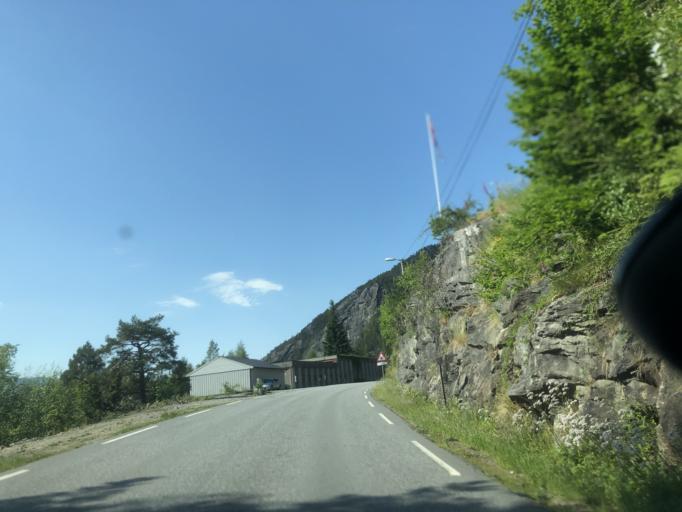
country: NO
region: Hordaland
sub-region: Jondal
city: Jondal
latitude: 60.2839
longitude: 6.2464
